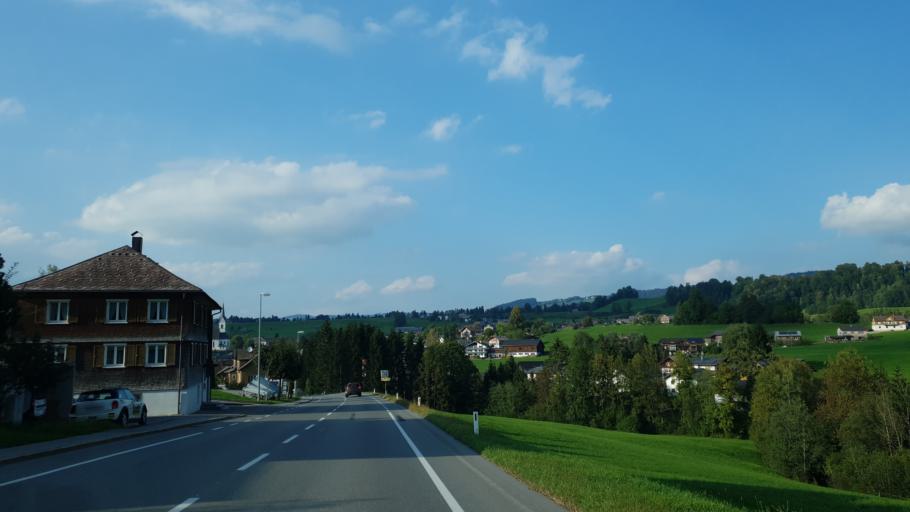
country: AT
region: Vorarlberg
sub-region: Politischer Bezirk Bregenz
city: Egg
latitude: 47.4244
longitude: 9.8979
